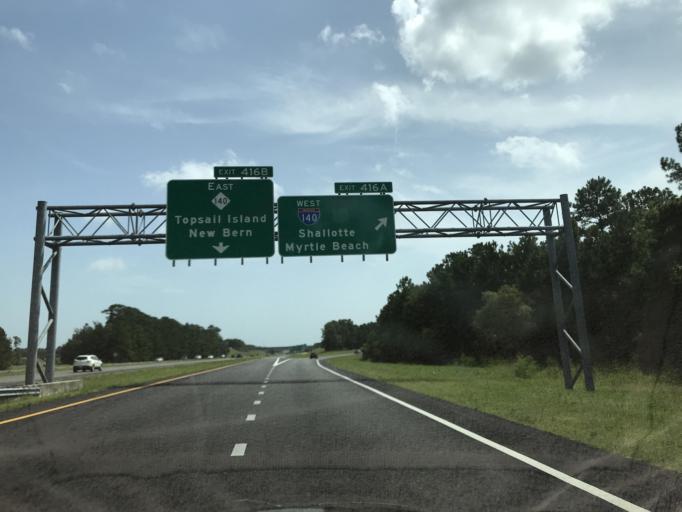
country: US
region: North Carolina
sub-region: New Hanover County
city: Skippers Corner
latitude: 34.3246
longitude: -77.8728
